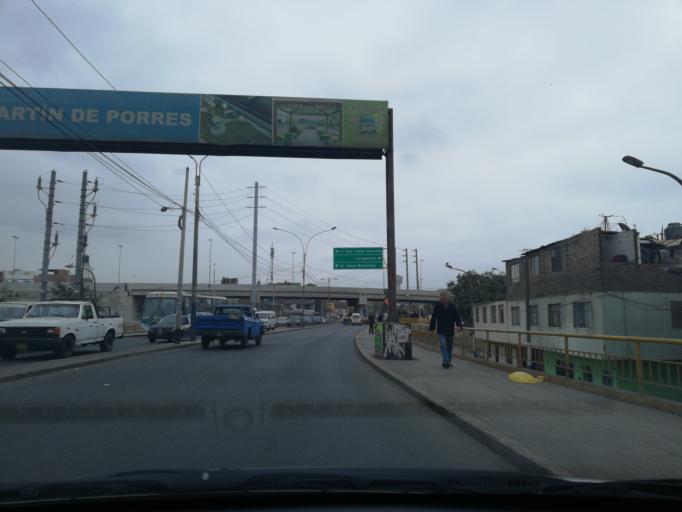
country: PE
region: Lima
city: Lima
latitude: -12.0342
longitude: -77.0653
